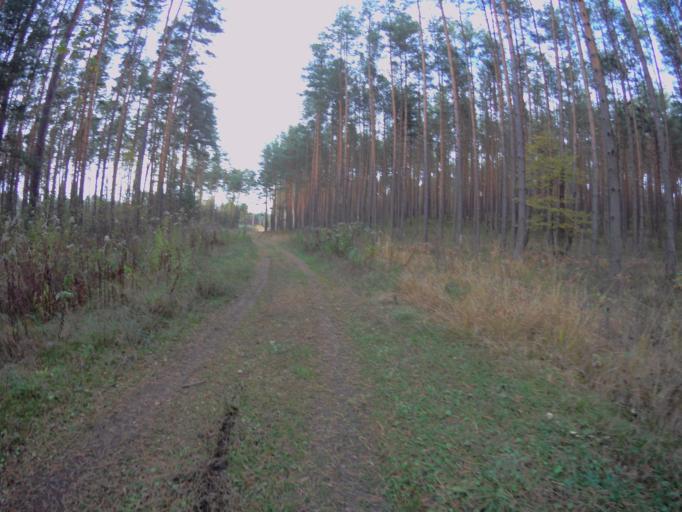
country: PL
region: Subcarpathian Voivodeship
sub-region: Powiat kolbuszowski
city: Lipnica
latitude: 50.3294
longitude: 21.9333
